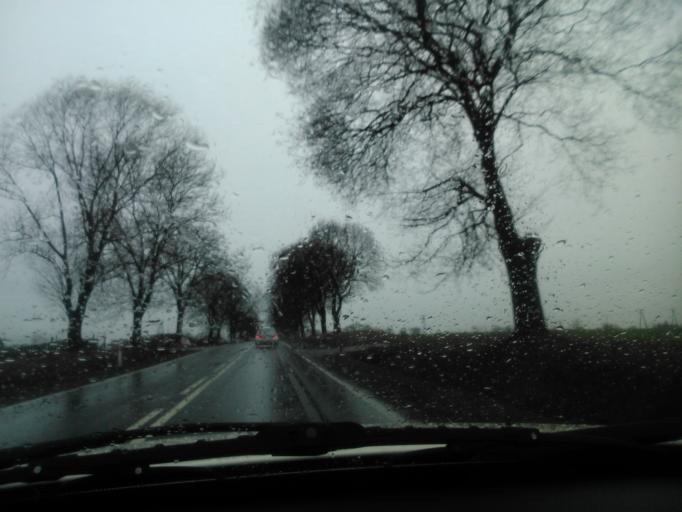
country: PL
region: Kujawsko-Pomorskie
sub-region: Powiat rypinski
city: Ostrowite
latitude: 53.0686
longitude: 19.3365
